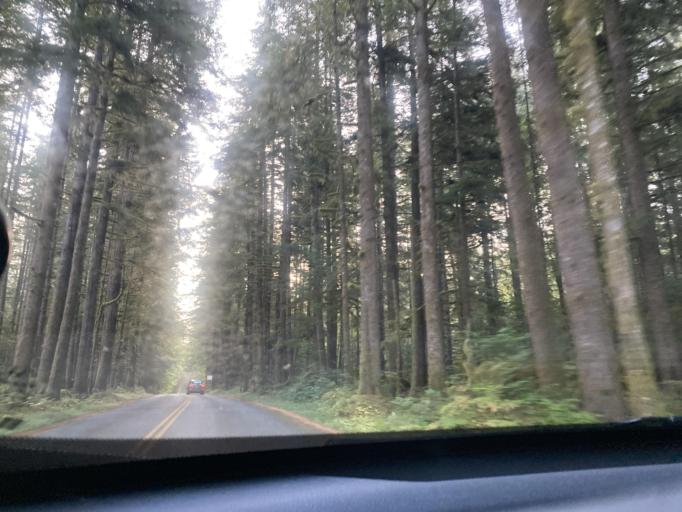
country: US
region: Washington
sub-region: Clallam County
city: Forks
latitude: 47.8163
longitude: -124.0541
